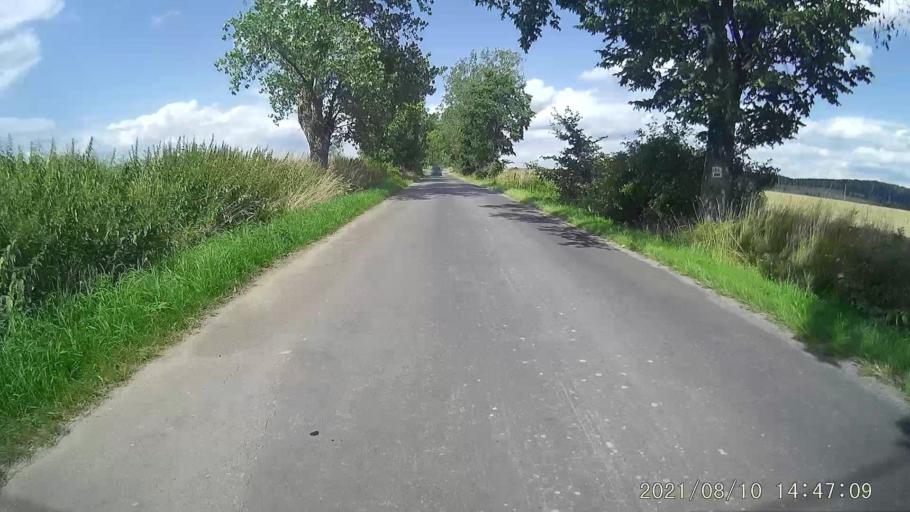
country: PL
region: Lower Silesian Voivodeship
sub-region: Powiat klodzki
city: Radkow
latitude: 50.5243
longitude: 16.4116
